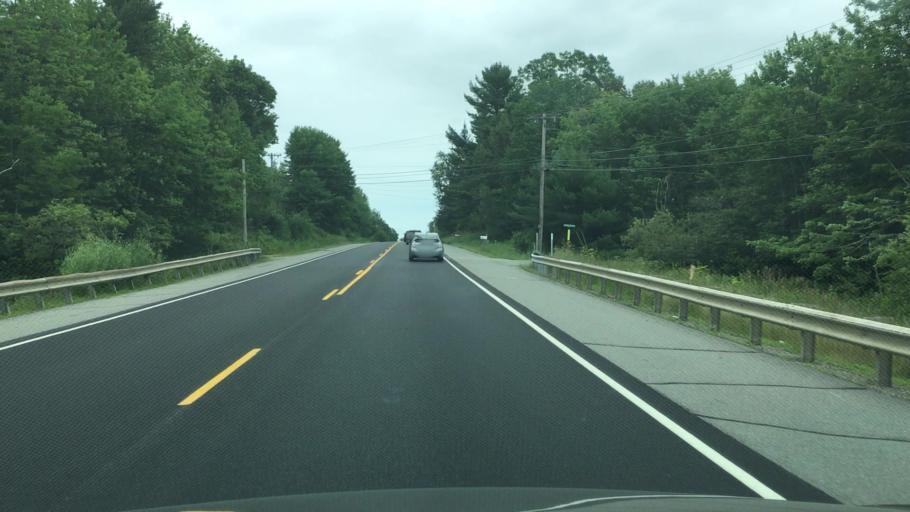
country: US
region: Maine
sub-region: Waldo County
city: Stockton Springs
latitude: 44.4996
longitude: -68.8298
